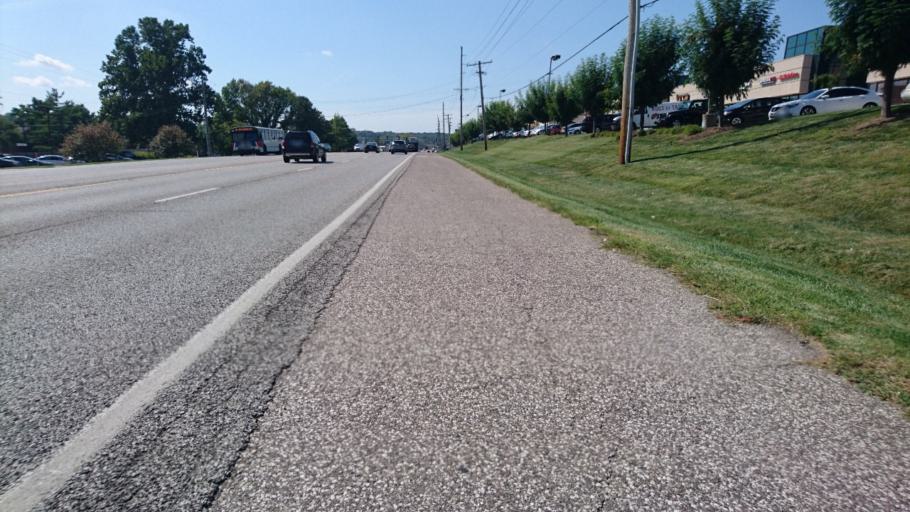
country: US
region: Missouri
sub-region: Saint Louis County
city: Manchester
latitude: 38.5940
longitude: -90.4970
